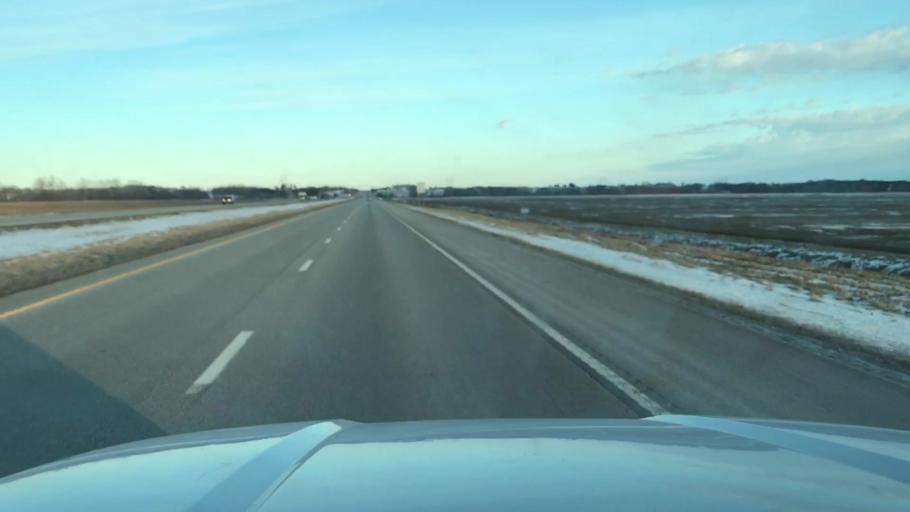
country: US
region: Missouri
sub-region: Buchanan County
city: Saint Joseph
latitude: 39.7479
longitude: -94.7423
